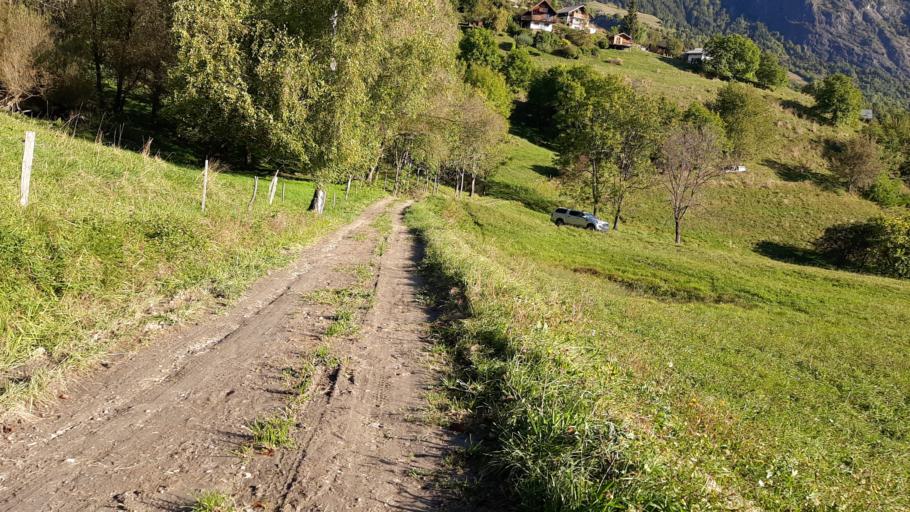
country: FR
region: Rhone-Alpes
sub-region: Departement de la Savoie
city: Saint-Jean-de-Maurienne
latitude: 45.2743
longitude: 6.3134
